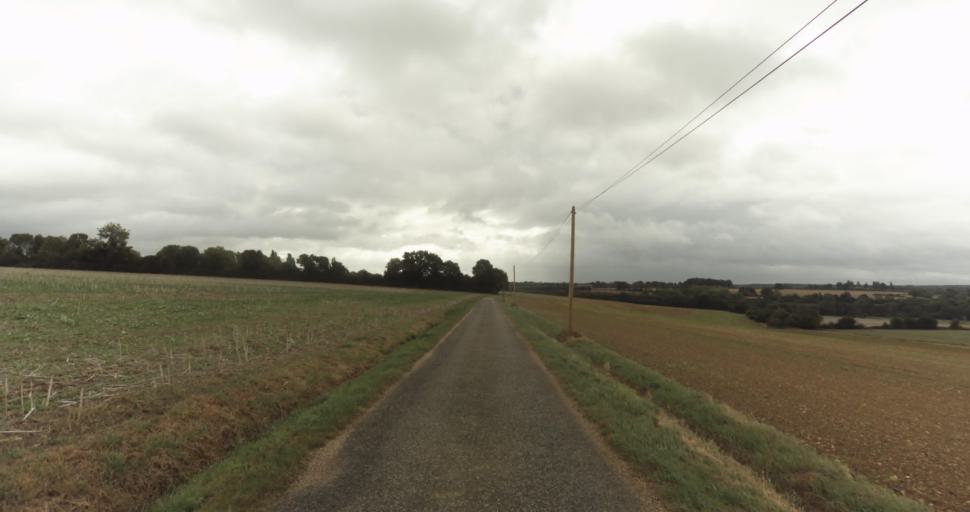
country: FR
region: Lower Normandy
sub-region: Departement de l'Orne
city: Sainte-Gauburge-Sainte-Colombe
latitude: 48.7330
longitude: 0.4556
